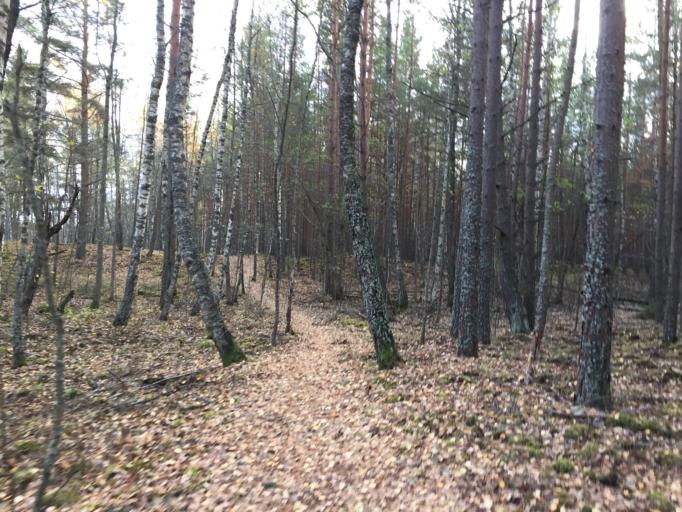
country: LV
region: Carnikava
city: Carnikava
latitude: 57.1517
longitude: 24.2588
